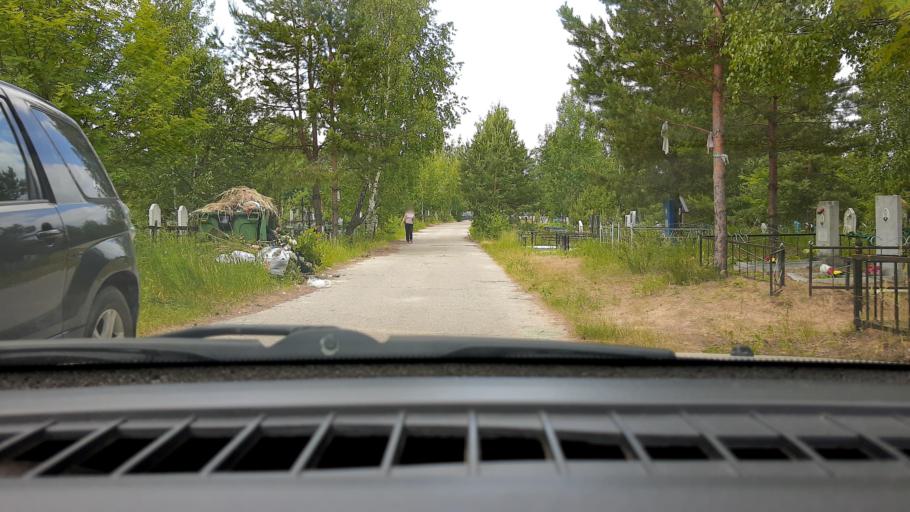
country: RU
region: Nizjnij Novgorod
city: Gorbatovka
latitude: 56.3594
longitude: 43.7615
